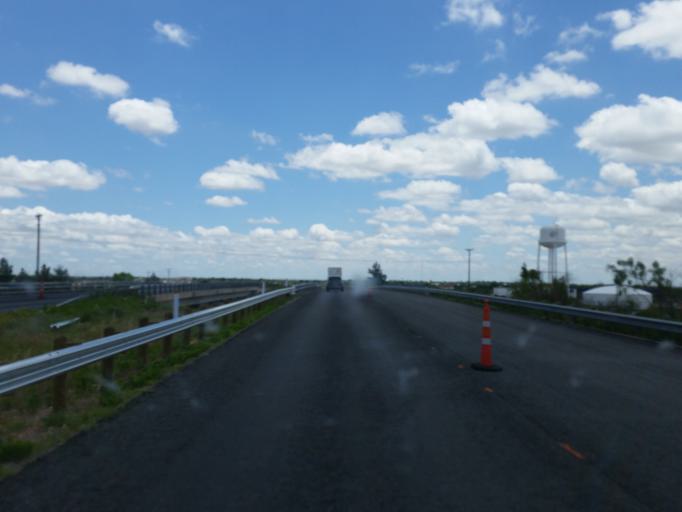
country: US
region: Texas
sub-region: Scurry County
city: Snyder
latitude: 32.7397
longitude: -100.9192
